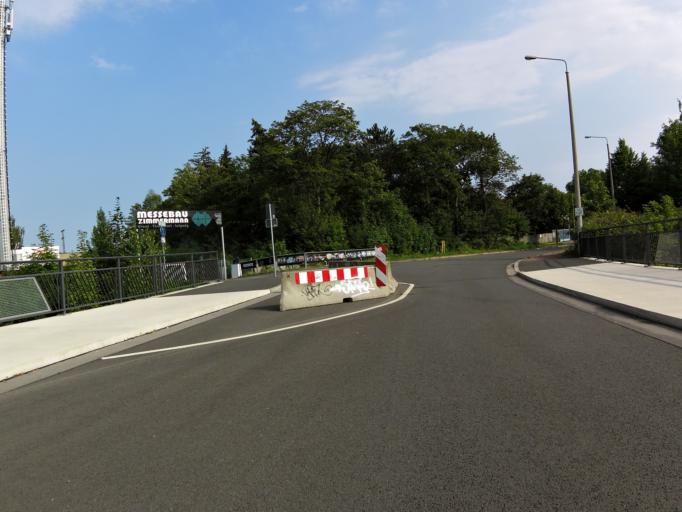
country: DE
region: Saxony
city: Rackwitz
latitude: 51.3873
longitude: 12.3897
